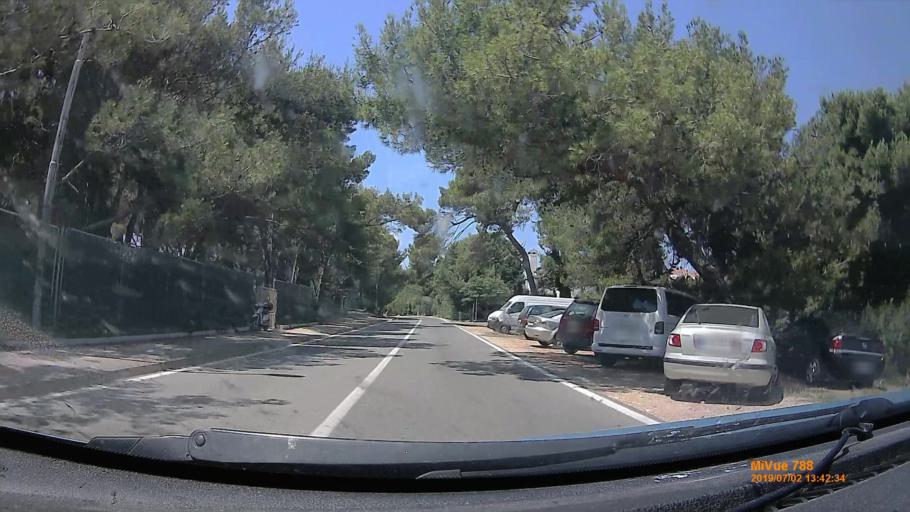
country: HR
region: Primorsko-Goranska
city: Mali Losinj
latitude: 44.5437
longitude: 14.4634
